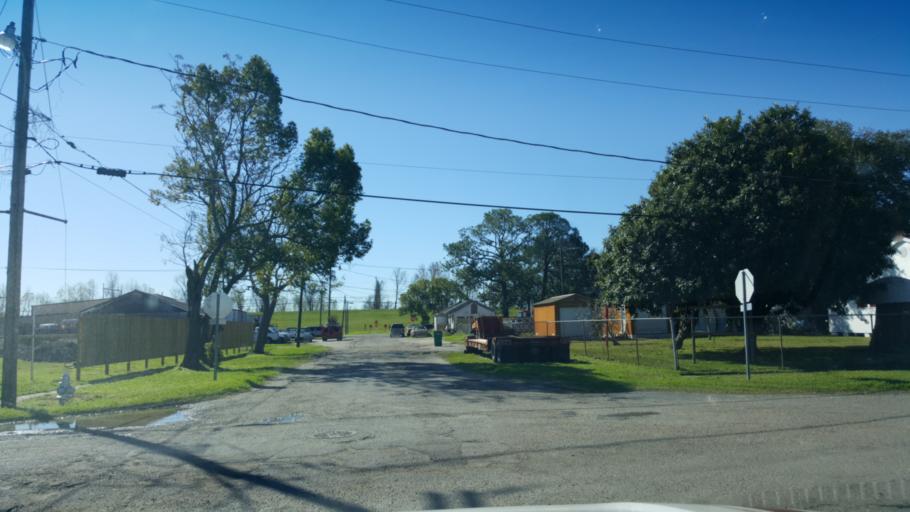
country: US
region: Louisiana
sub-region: Jefferson Parish
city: Kenner
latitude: 29.9758
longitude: -90.2539
